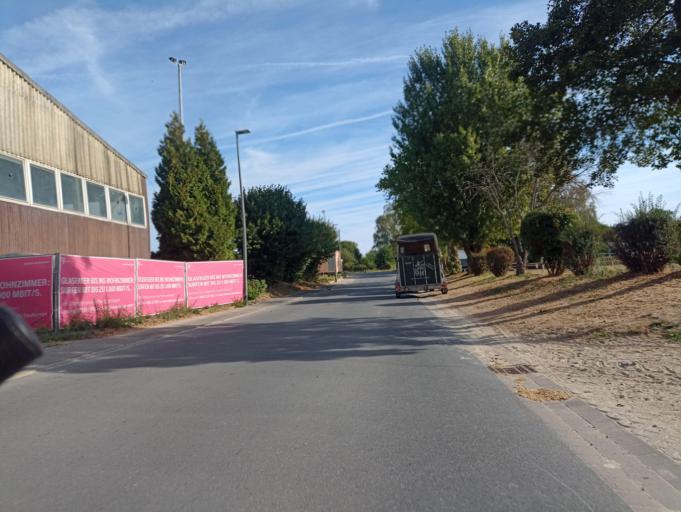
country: DE
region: Hesse
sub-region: Regierungsbezirk Darmstadt
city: Oberursel
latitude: 50.1991
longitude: 8.6054
